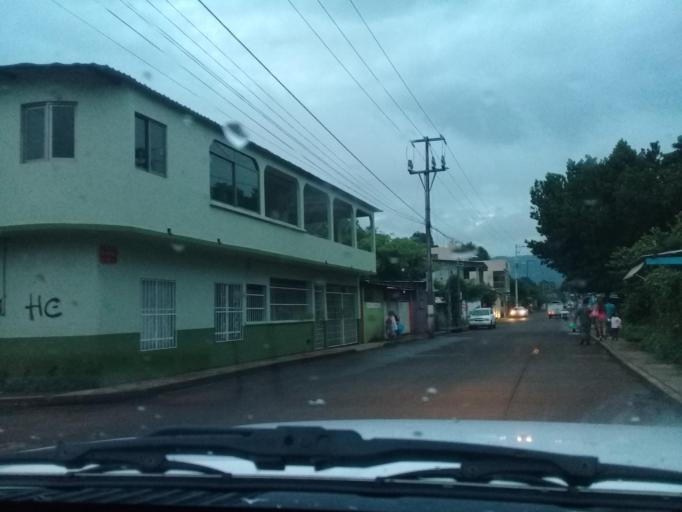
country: MX
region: Veracruz
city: San Andres Tuxtla
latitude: 18.4413
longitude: -95.2218
